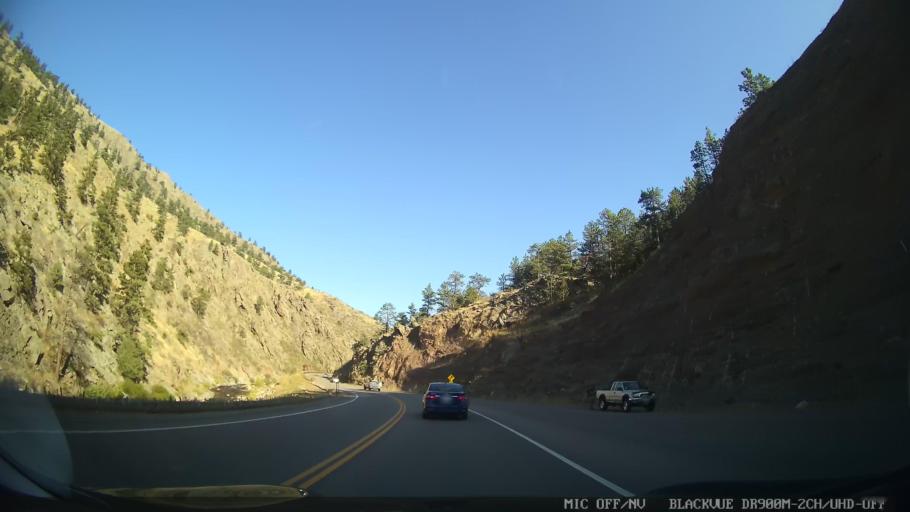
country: US
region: Colorado
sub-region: Boulder County
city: Lyons
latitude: 40.4217
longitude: -105.2879
